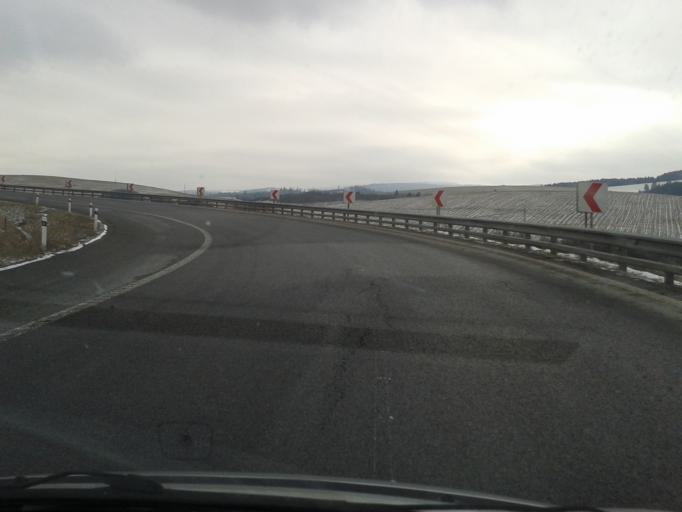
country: SK
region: Zilinsky
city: Tvrdosin
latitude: 49.3441
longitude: 19.5779
